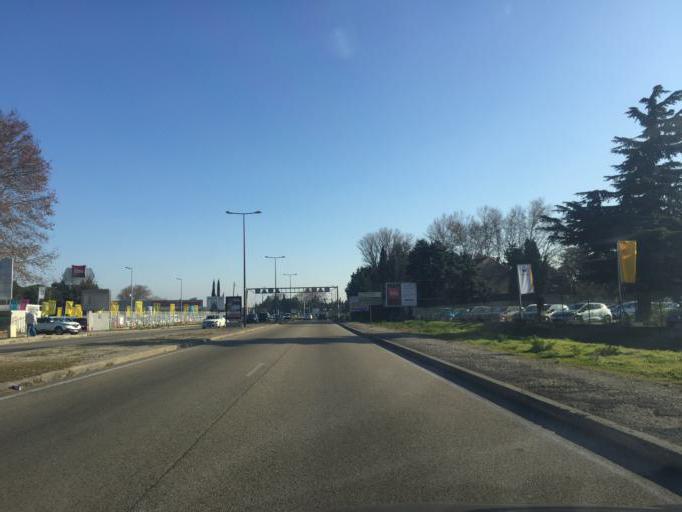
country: FR
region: Provence-Alpes-Cote d'Azur
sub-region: Departement du Vaucluse
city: Montfavet
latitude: 43.9262
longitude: 4.8461
